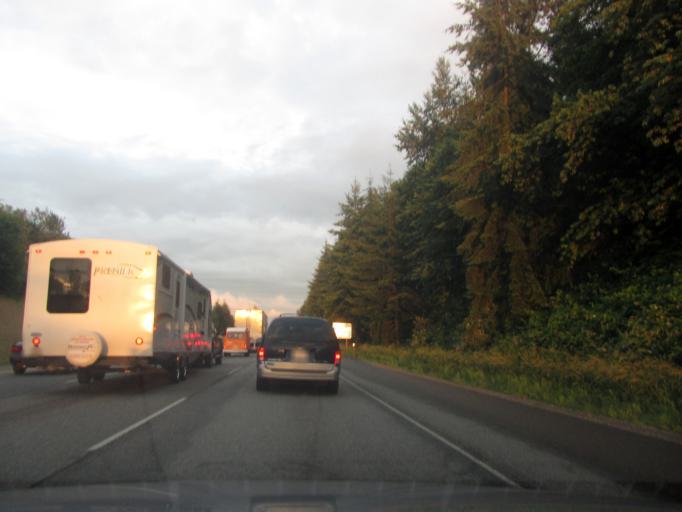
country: CA
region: British Columbia
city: Aldergrove
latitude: 49.1096
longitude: -122.5140
